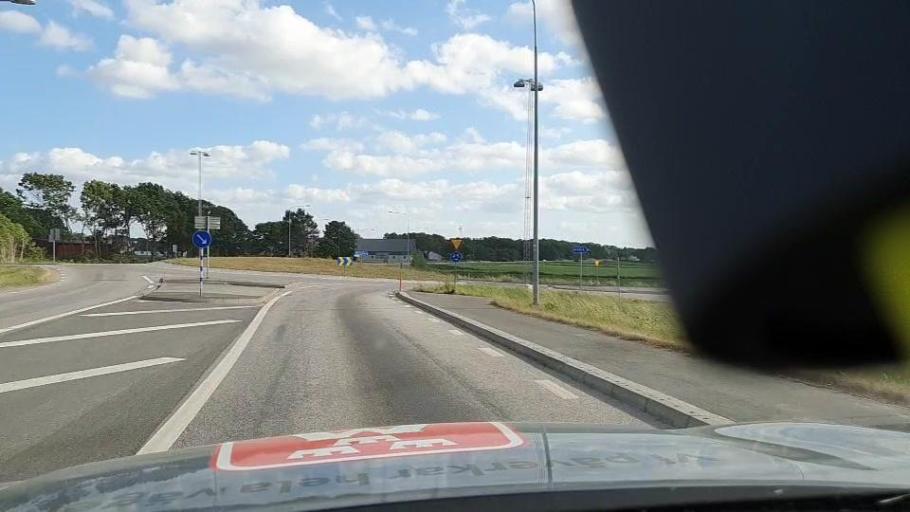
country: SE
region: Blekinge
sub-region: Karlshamns Kommun
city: Morrum
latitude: 56.1125
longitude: 14.6751
